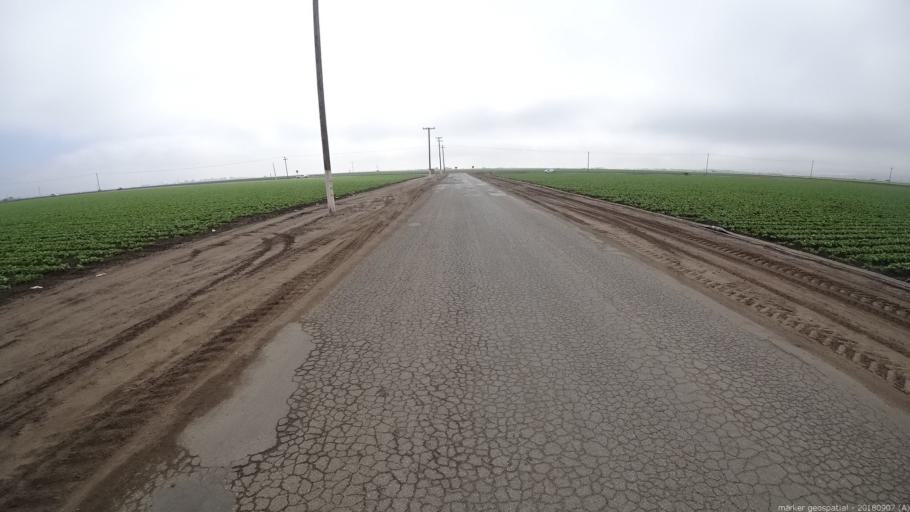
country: US
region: California
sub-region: Monterey County
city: Salinas
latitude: 36.6390
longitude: -121.6393
